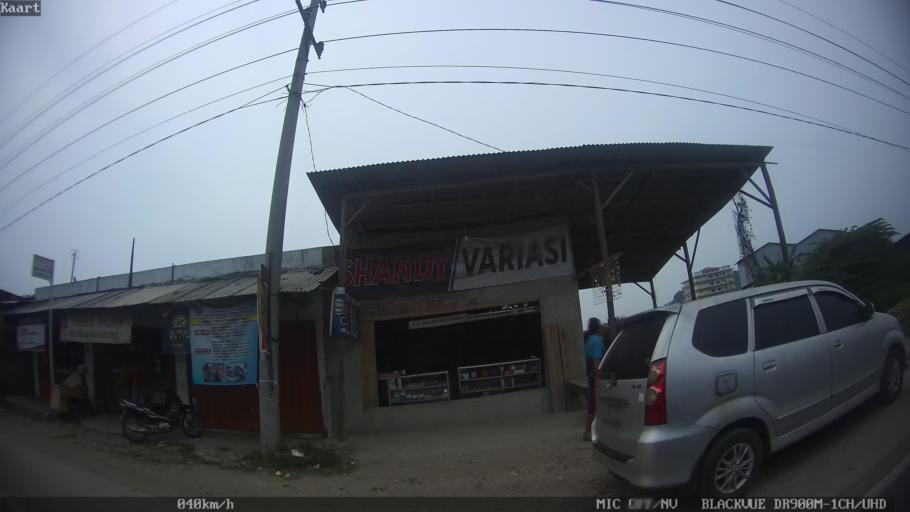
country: ID
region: Lampung
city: Panjang
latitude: -5.4163
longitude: 105.3443
